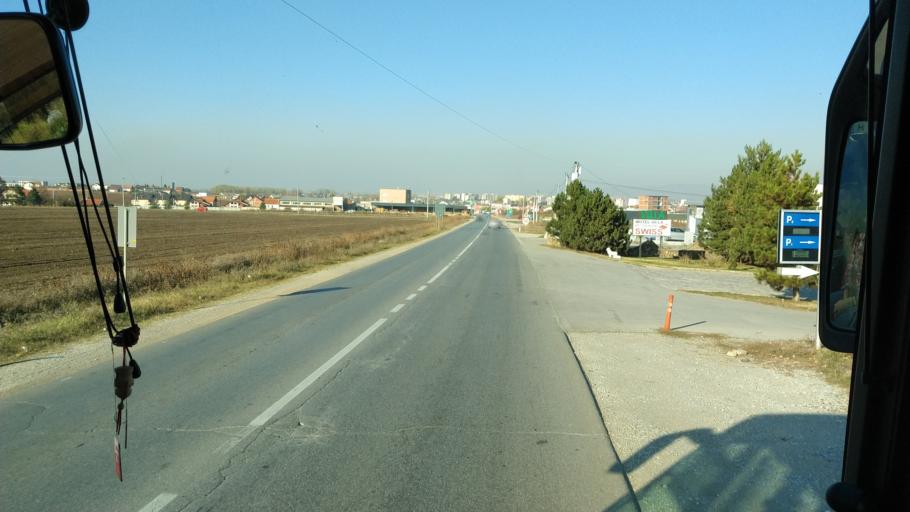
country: XK
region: Pristina
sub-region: Lipjan
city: Lipljan
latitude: 42.5020
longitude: 21.1095
